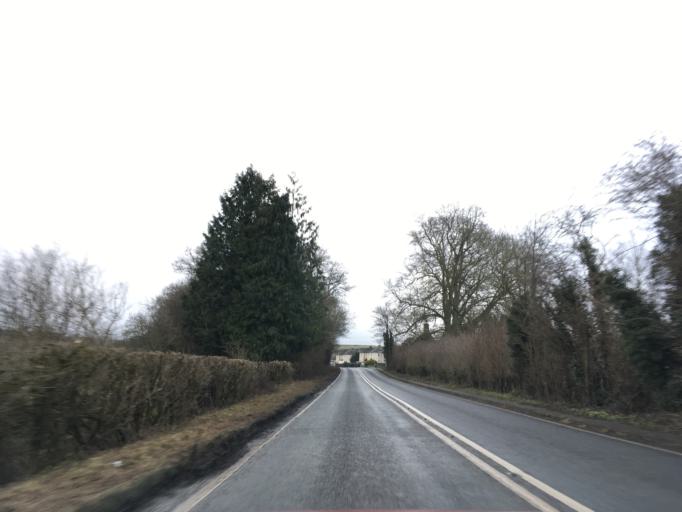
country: GB
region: England
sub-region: Gloucestershire
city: Cirencester
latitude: 51.7663
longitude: -1.9720
